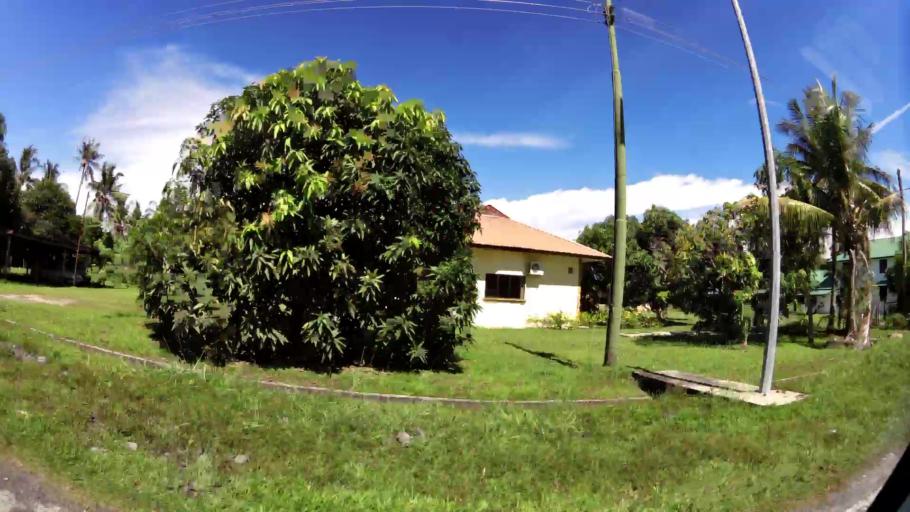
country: BN
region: Brunei and Muara
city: Bandar Seri Begawan
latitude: 5.0058
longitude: 115.0586
